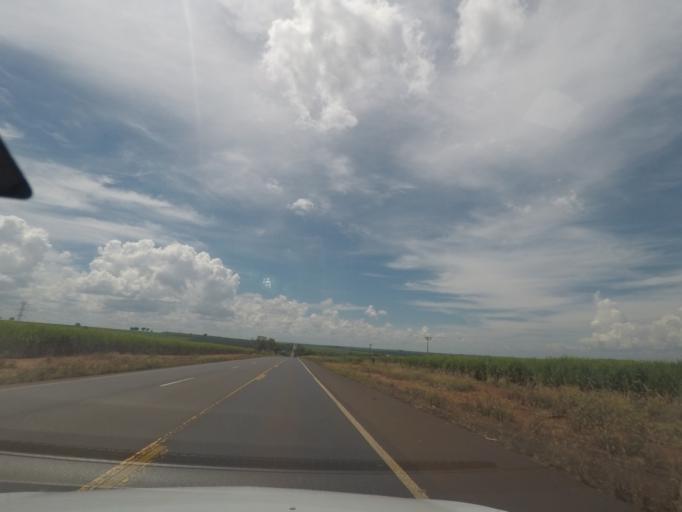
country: BR
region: Sao Paulo
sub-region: Barretos
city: Barretos
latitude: -20.2700
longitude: -48.6733
